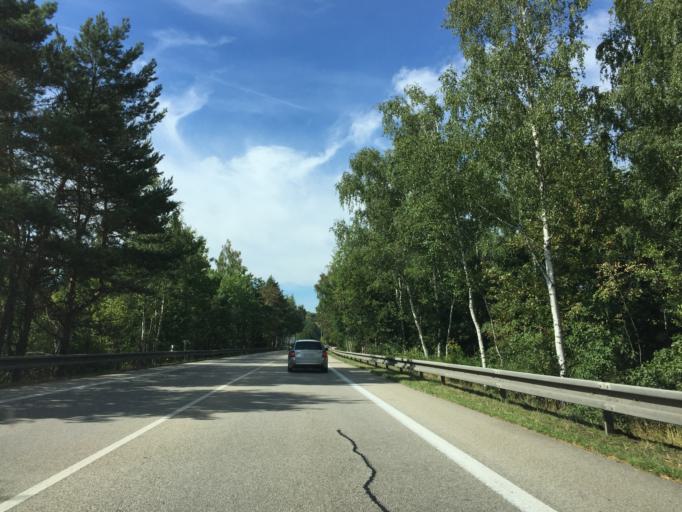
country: CZ
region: Central Bohemia
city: Votice
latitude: 49.6482
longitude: 14.6367
